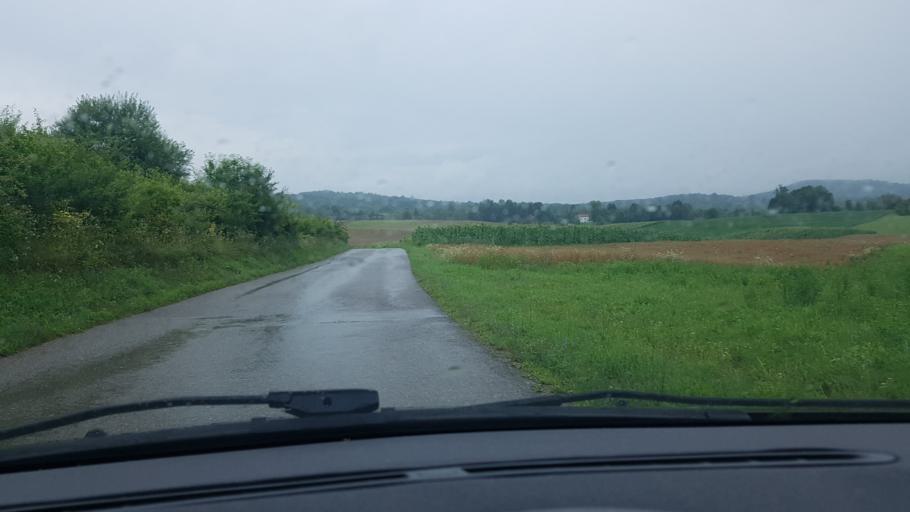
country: BA
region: Federation of Bosnia and Herzegovina
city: Trzacka Rastela
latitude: 44.9895
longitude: 15.6689
